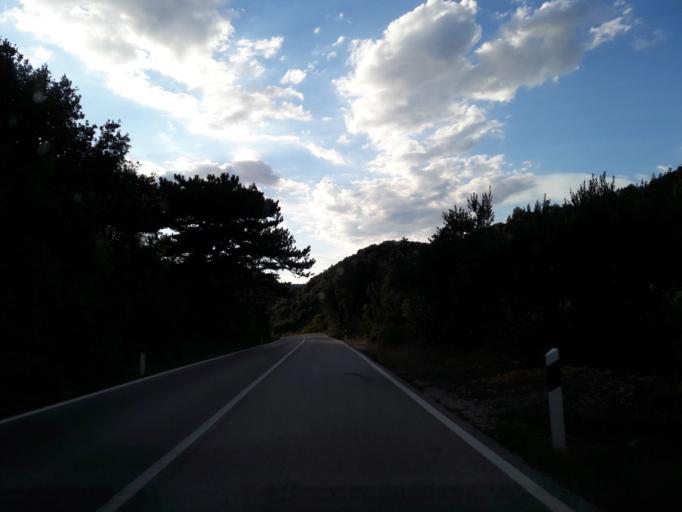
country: HR
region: Dubrovacko-Neretvanska
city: Orebic
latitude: 42.9857
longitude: 17.2752
